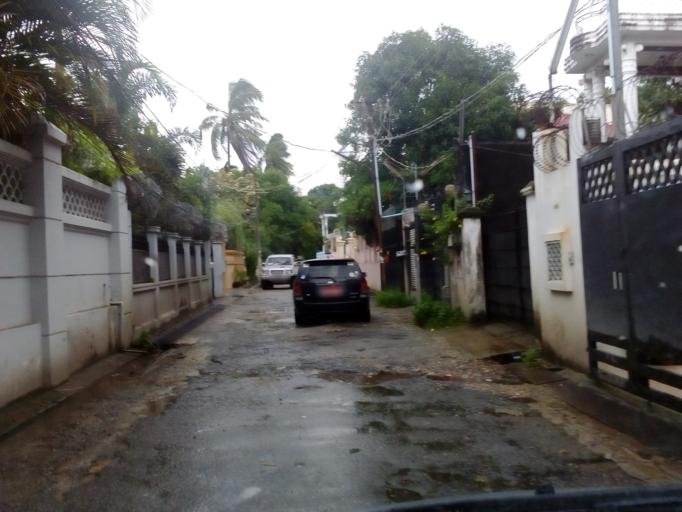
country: MM
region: Yangon
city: Yangon
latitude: 16.8174
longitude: 96.1504
